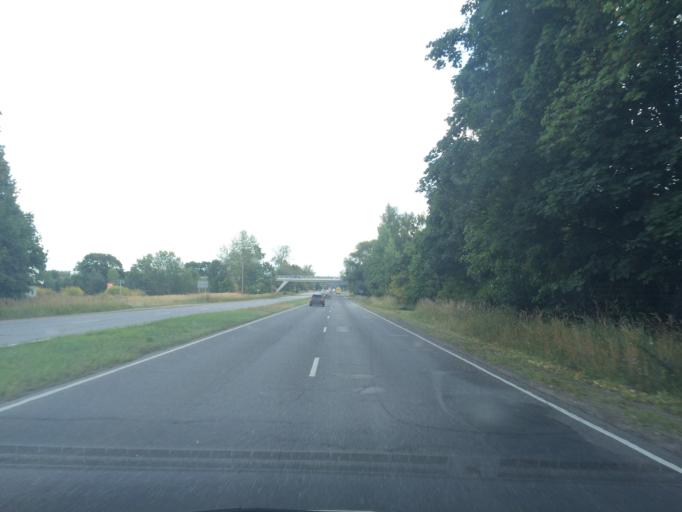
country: LV
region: Salaspils
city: Salaspils
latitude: 56.8598
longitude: 24.3071
